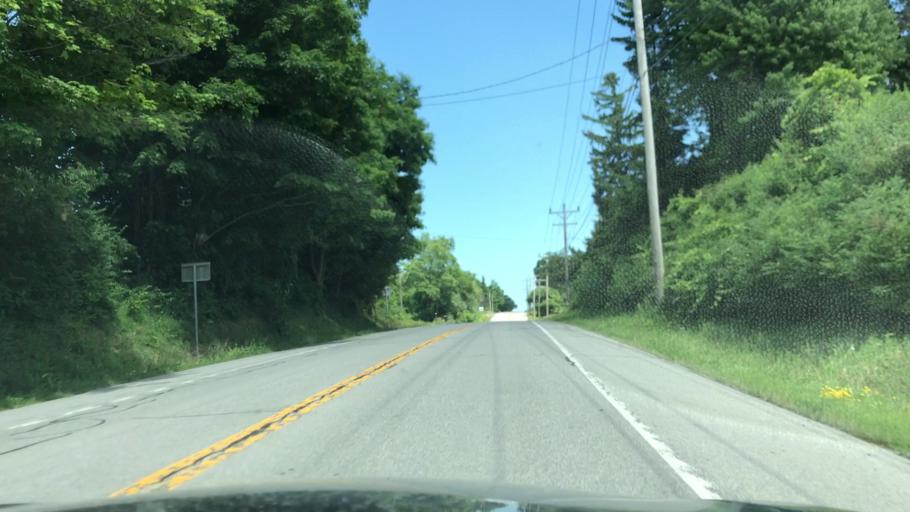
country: US
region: New York
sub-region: Wyoming County
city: Perry
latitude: 42.7465
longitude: -78.0331
